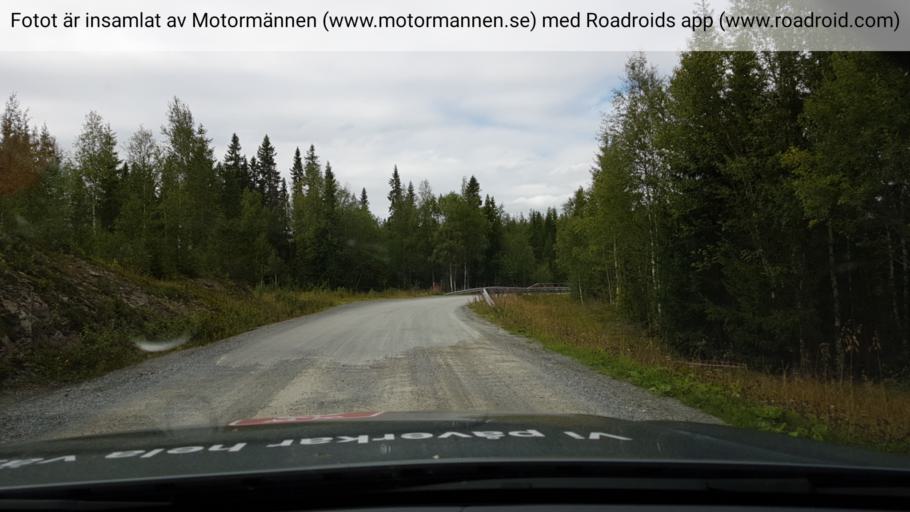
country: SE
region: Jaemtland
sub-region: Krokoms Kommun
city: Valla
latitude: 63.6622
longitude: 13.7345
